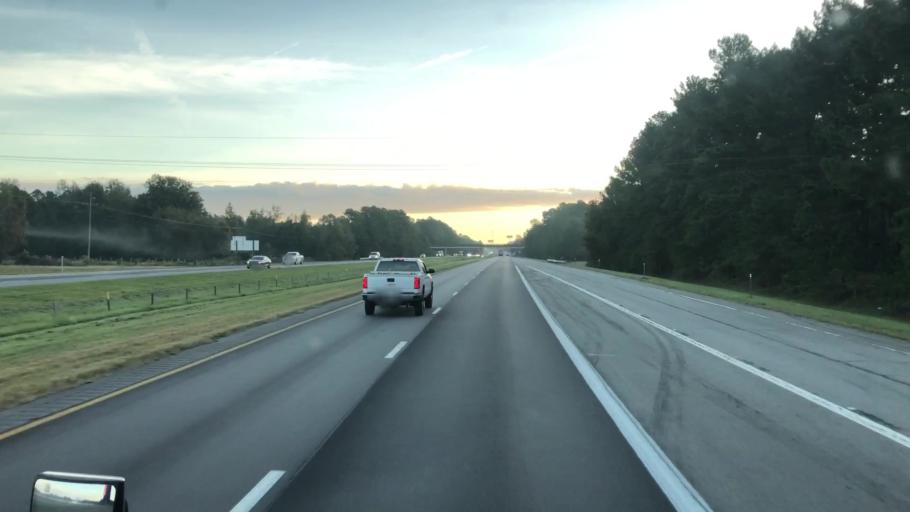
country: US
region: South Carolina
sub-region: Clarendon County
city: Manning
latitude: 33.5909
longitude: -80.3522
